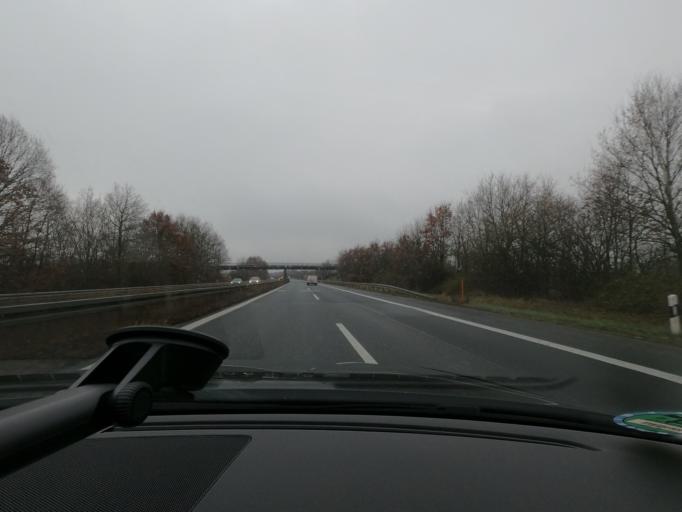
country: DE
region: Bavaria
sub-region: Upper Franconia
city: Altendorf
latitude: 49.8123
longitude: 11.0123
